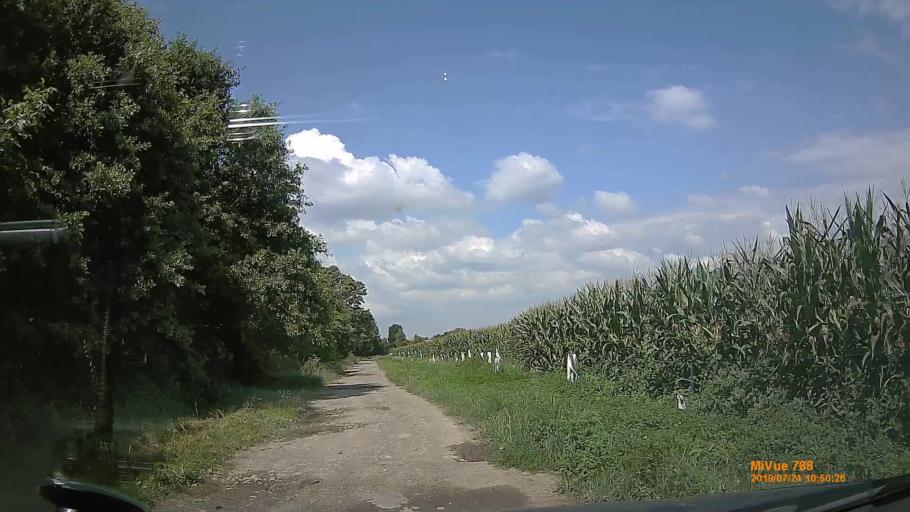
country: UA
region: Zakarpattia
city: Berehove
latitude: 48.1959
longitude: 22.5596
